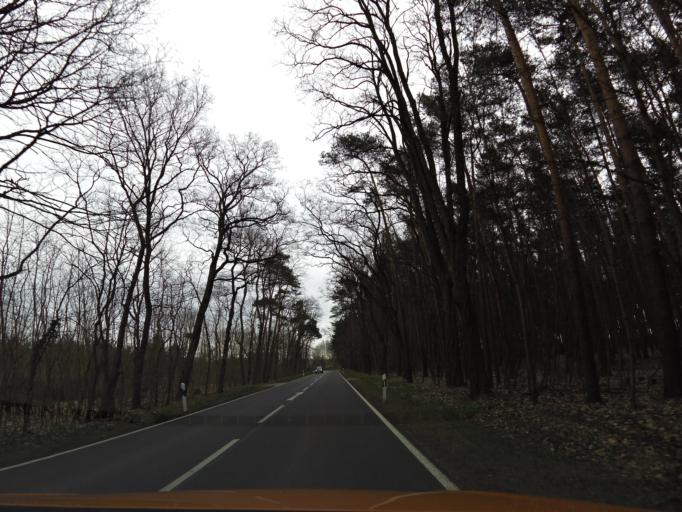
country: DE
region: Brandenburg
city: Bruck
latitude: 52.1653
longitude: 12.7240
